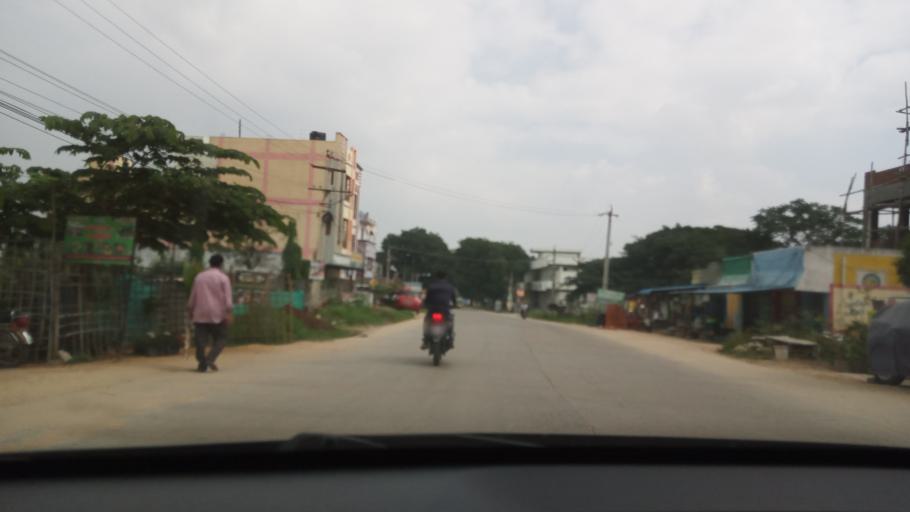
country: IN
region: Andhra Pradesh
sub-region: Chittoor
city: Madanapalle
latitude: 13.6529
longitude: 78.8061
